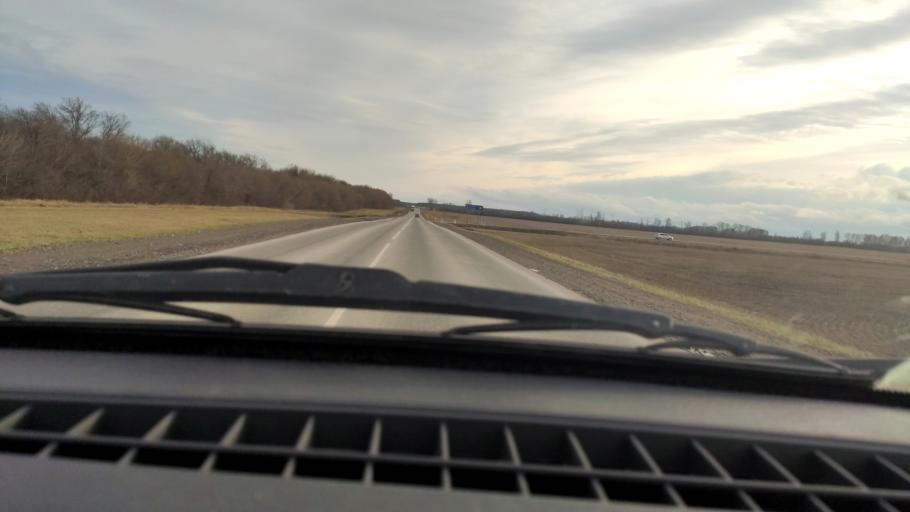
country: RU
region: Bashkortostan
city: Davlekanovo
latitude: 54.2760
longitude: 55.1039
